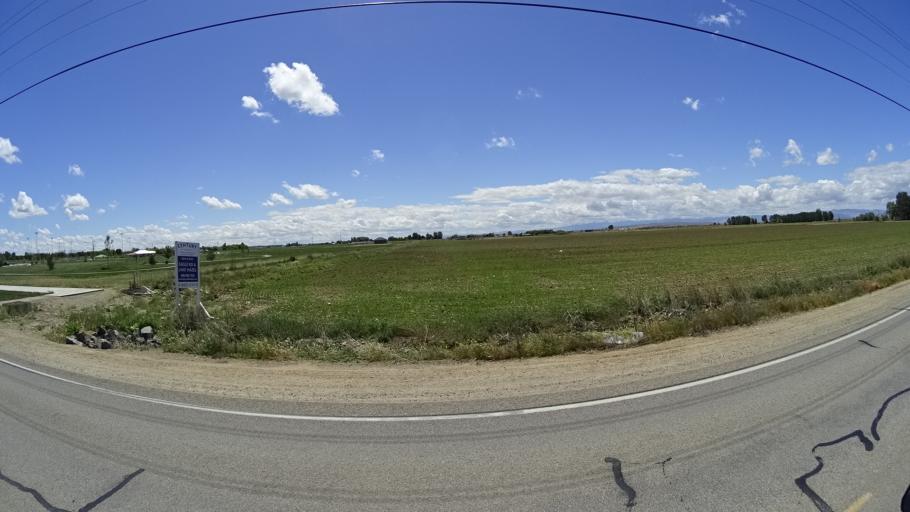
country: US
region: Idaho
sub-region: Ada County
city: Meridian
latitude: 43.5466
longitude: -116.3693
